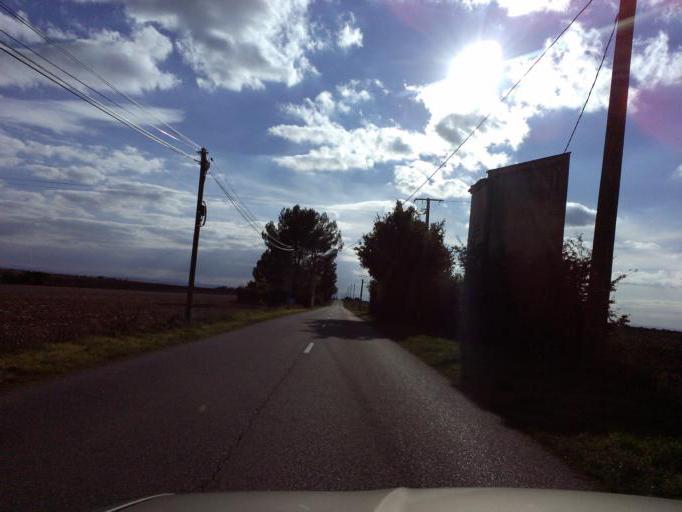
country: FR
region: Provence-Alpes-Cote d'Azur
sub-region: Departement des Alpes-de-Haute-Provence
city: Valensole
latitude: 43.8569
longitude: 6.0000
